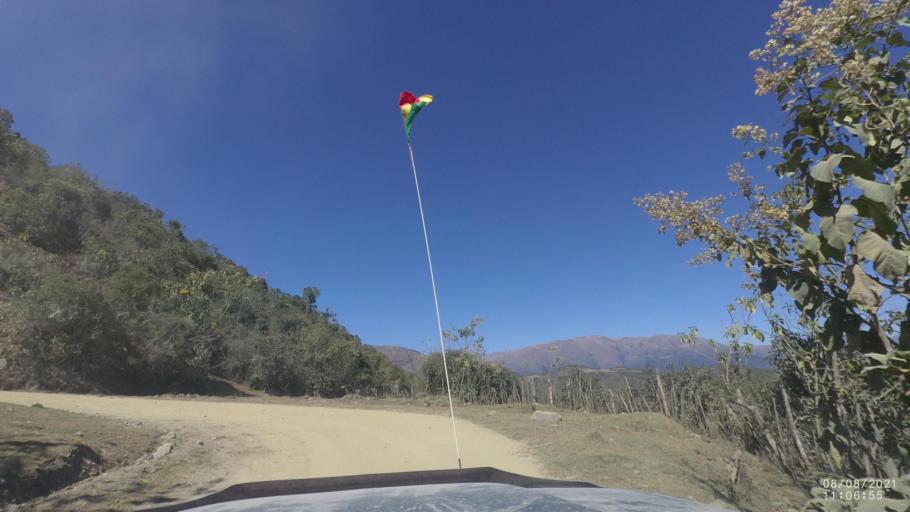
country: BO
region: Cochabamba
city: Colchani
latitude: -16.7660
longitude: -66.6840
